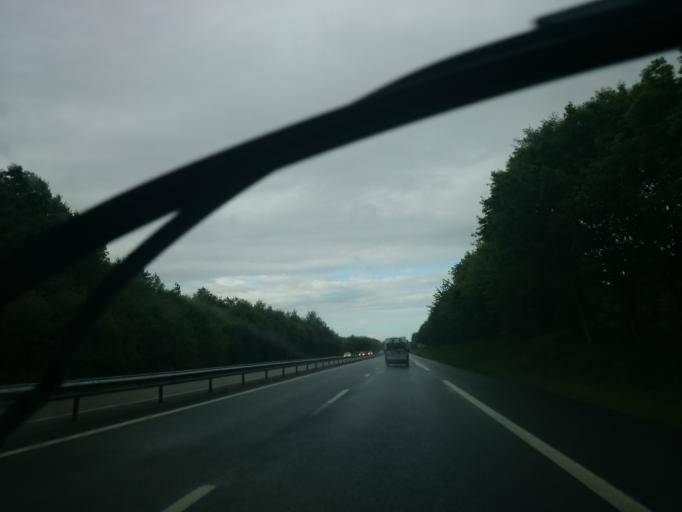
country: FR
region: Brittany
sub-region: Departement du Morbihan
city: Campeneac
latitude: 47.9276
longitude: -2.3304
